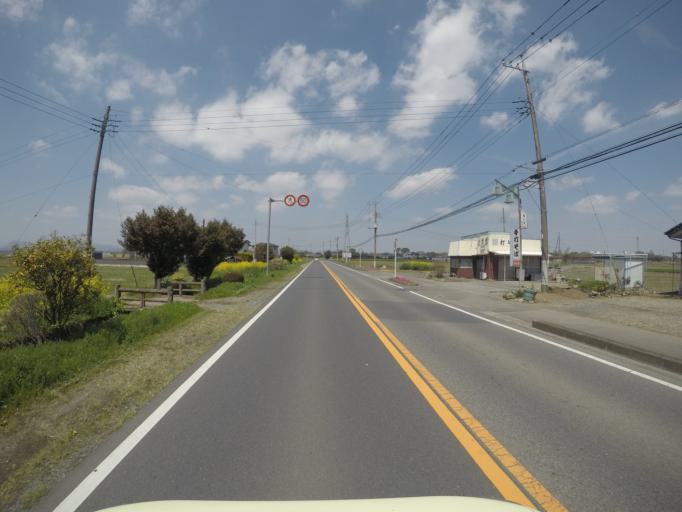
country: JP
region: Tochigi
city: Mibu
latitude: 36.4341
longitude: 139.7928
